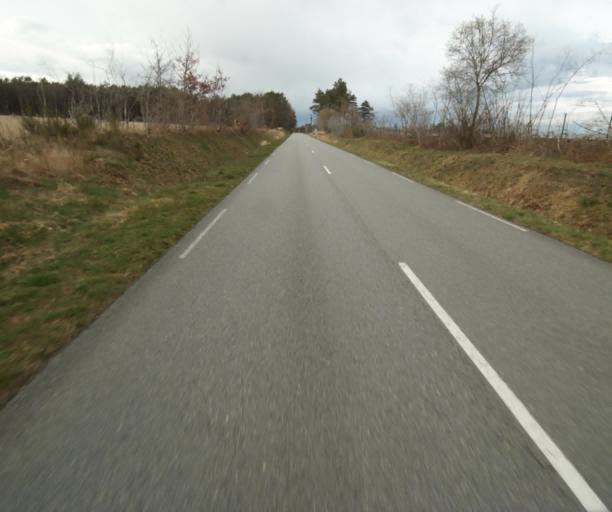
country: FR
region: Limousin
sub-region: Departement de la Correze
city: Saint-Privat
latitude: 45.2044
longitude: 2.0045
